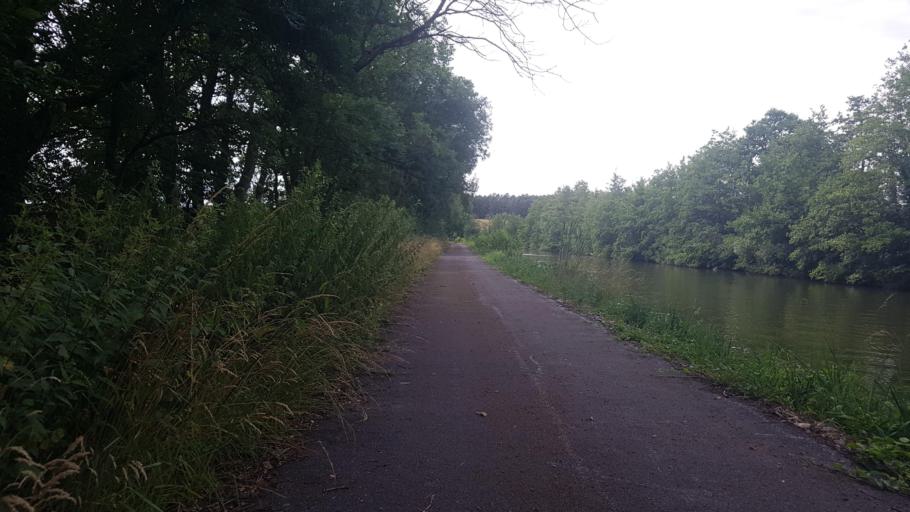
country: FR
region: Lorraine
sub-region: Departement de la Moselle
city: Dieuze
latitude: 48.6967
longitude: 6.7425
